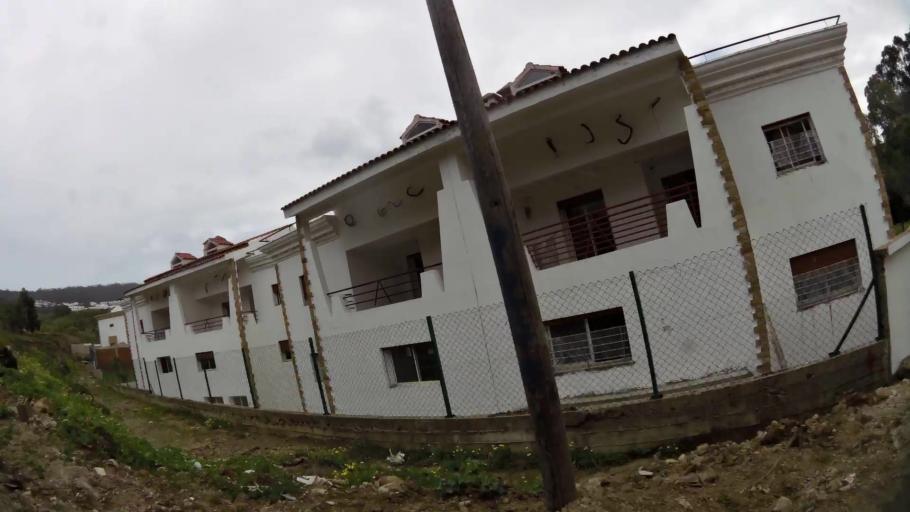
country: MA
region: Tanger-Tetouan
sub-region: Tanger-Assilah
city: Boukhalef
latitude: 35.7781
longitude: -5.8655
